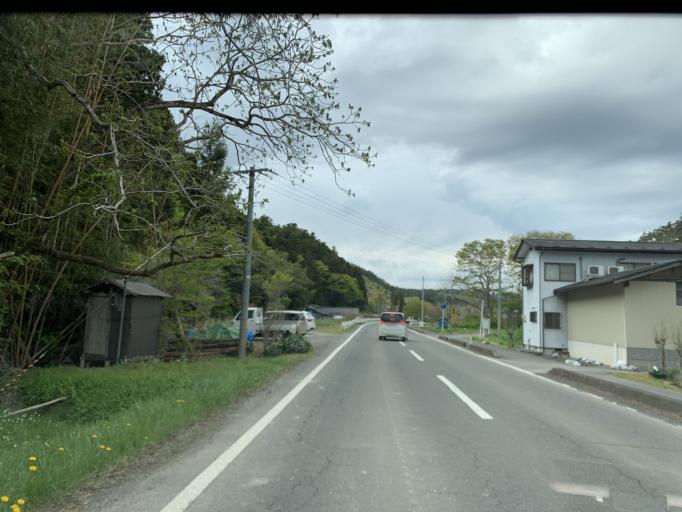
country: JP
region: Iwate
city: Ichinoseki
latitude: 38.7819
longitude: 141.3272
